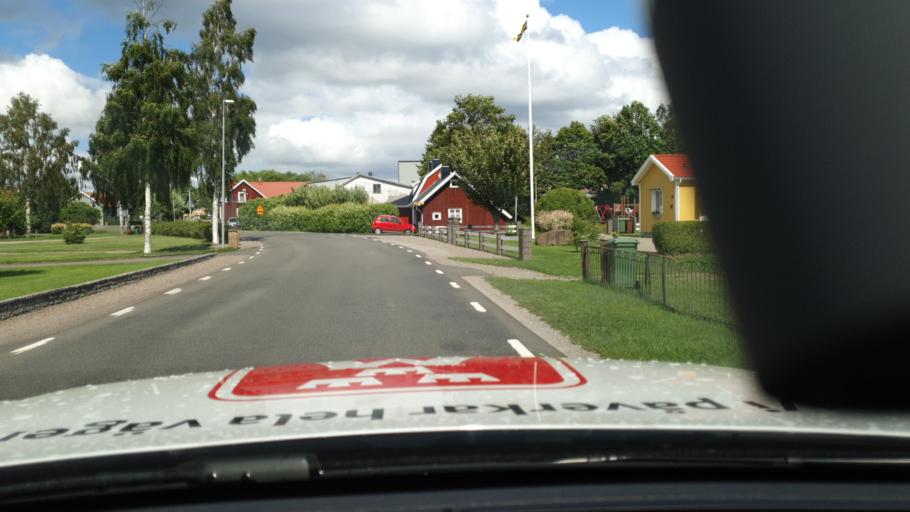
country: SE
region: Vaestra Goetaland
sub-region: Falkopings Kommun
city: Akarp
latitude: 58.3043
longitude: 13.6052
